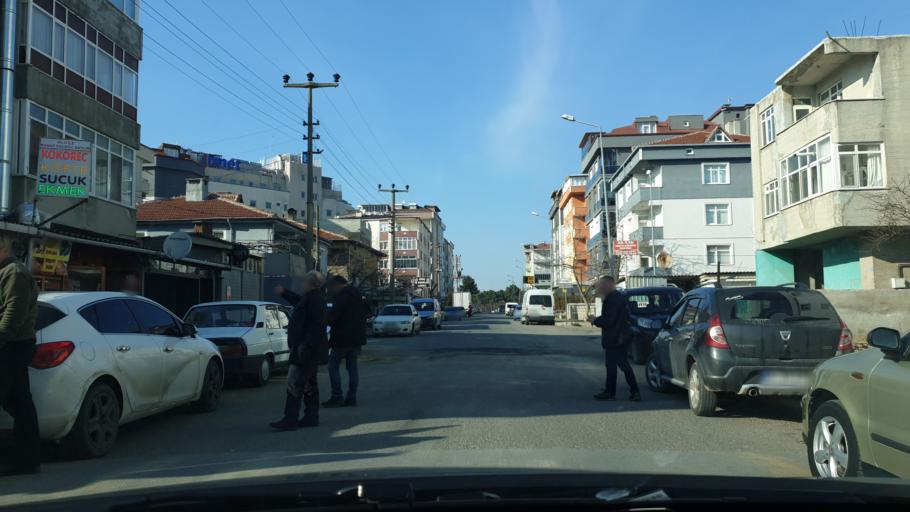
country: TR
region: Tekirdag
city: Cerkezkoey
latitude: 41.2924
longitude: 27.9962
